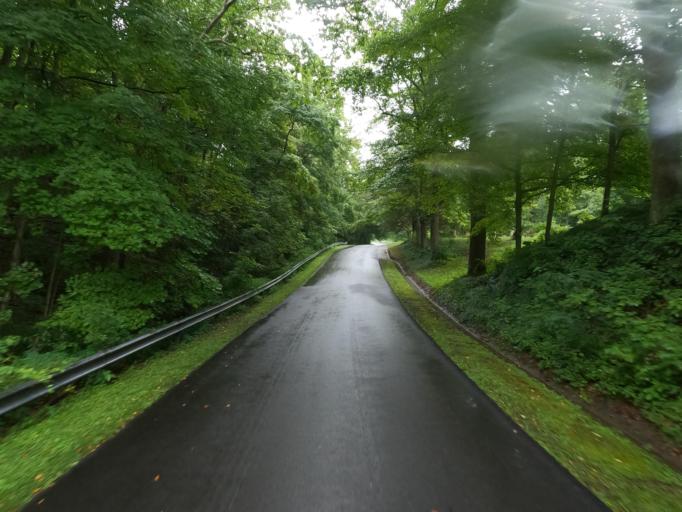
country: US
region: West Virginia
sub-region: Marion County
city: Fairmont
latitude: 39.5158
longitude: -80.0972
